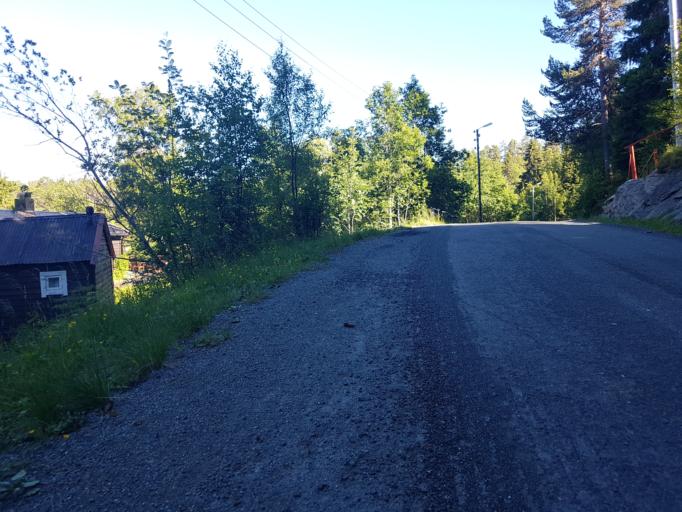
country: NO
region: Sor-Trondelag
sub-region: Trondheim
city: Trondheim
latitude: 63.4306
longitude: 10.2765
